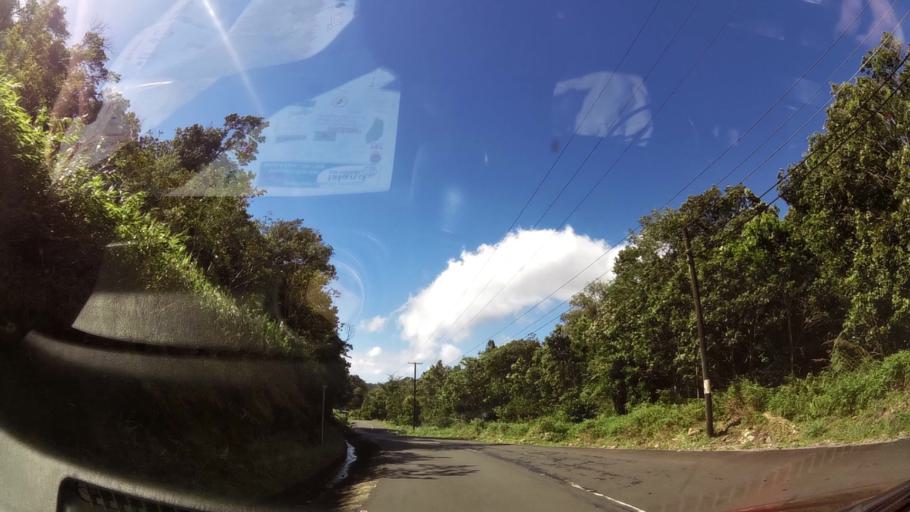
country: DM
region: Saint Paul
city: Pont Casse
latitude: 15.3743
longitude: -61.3448
